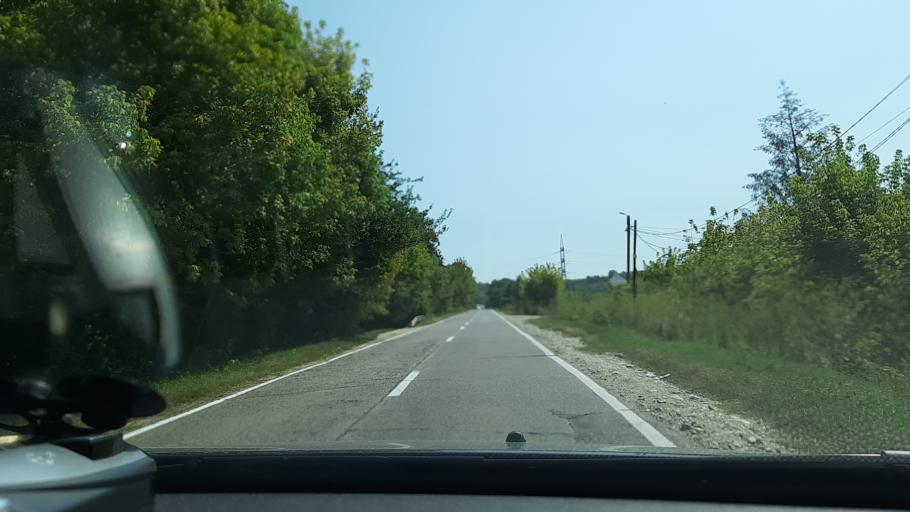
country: RO
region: Gorj
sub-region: Comuna Targu Carbunesti
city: Targu Carbunesti
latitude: 44.9457
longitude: 23.5205
